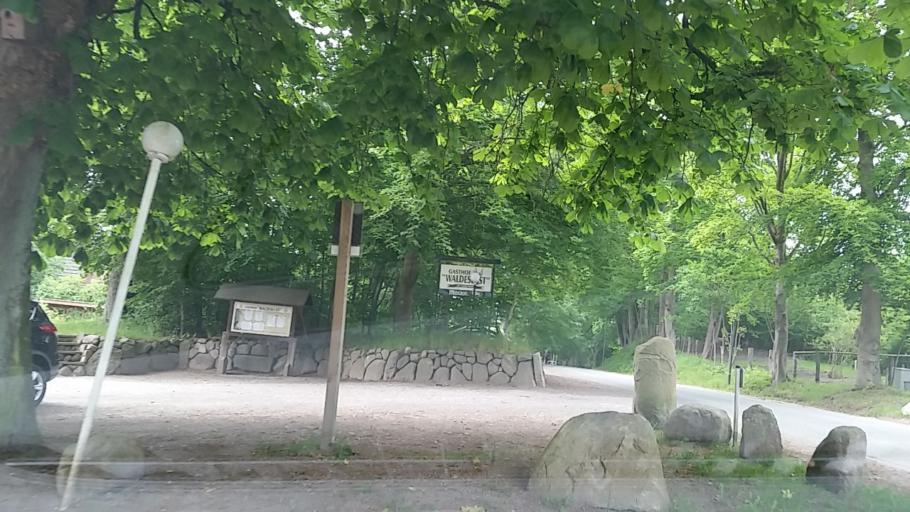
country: DE
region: Schleswig-Holstein
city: Dahmker
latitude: 53.6054
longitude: 10.4455
